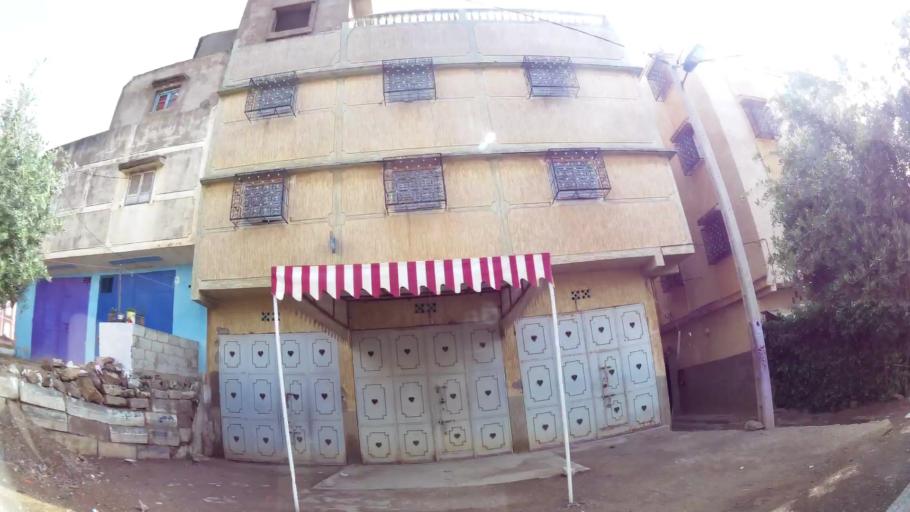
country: MA
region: Rabat-Sale-Zemmour-Zaer
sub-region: Khemisset
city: Tiflet
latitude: 33.8952
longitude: -6.3158
